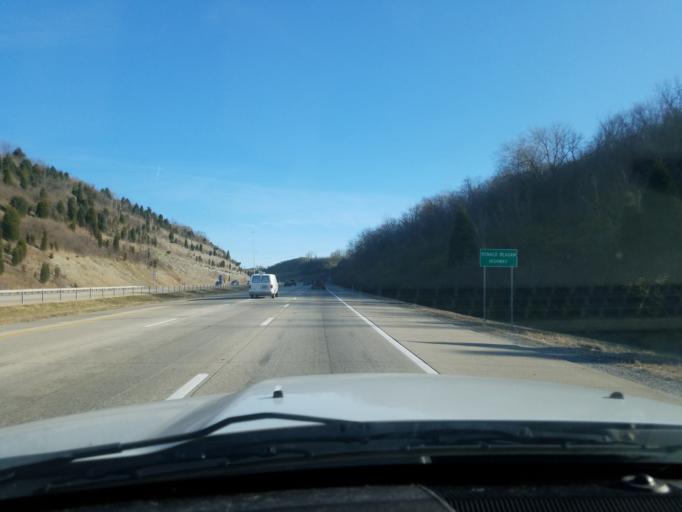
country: US
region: Kentucky
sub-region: Campbell County
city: Highland Heights
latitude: 39.0254
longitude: -84.4771
